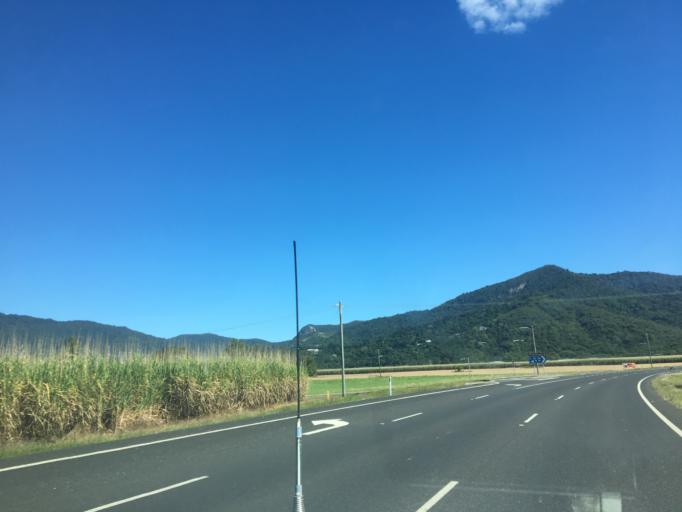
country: AU
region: Queensland
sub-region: Cairns
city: Redlynch
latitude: -16.8507
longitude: 145.7068
